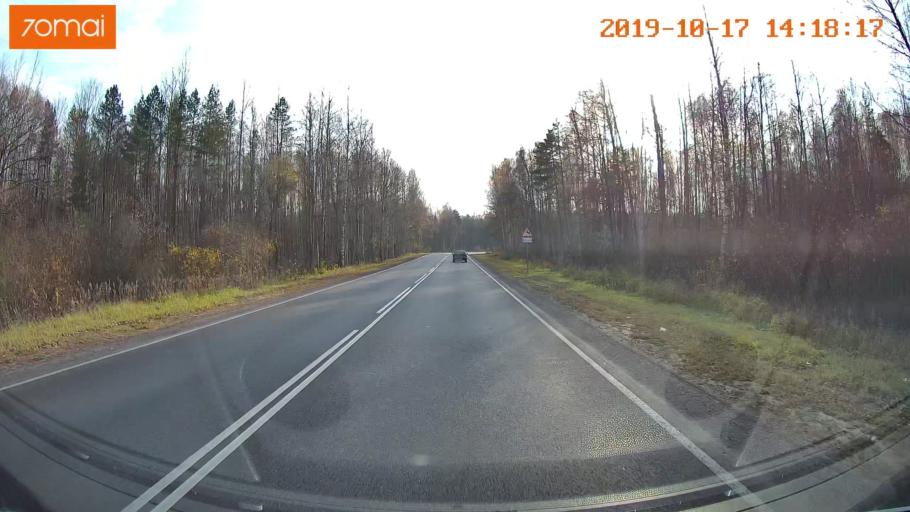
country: RU
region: Rjazan
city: Spas-Klepiki
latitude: 55.0649
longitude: 40.0317
